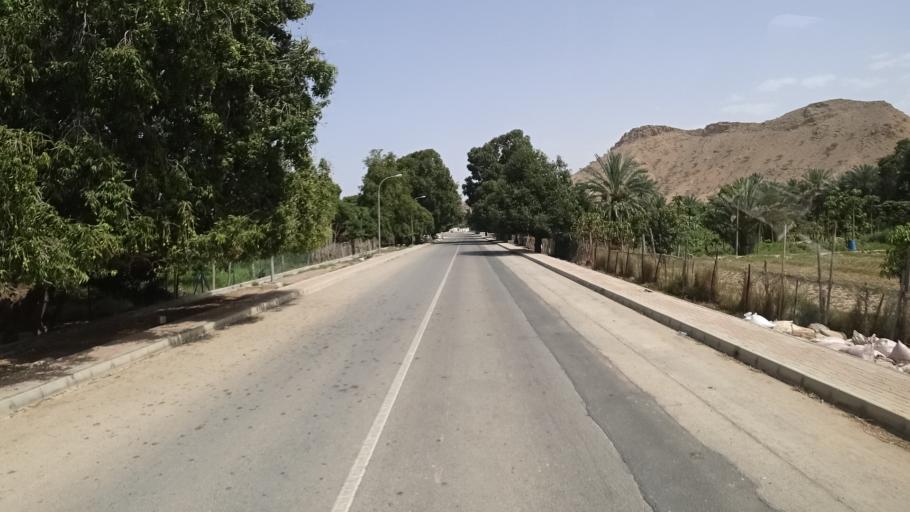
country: OM
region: Muhafazat Masqat
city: Muscat
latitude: 23.1693
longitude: 58.9184
